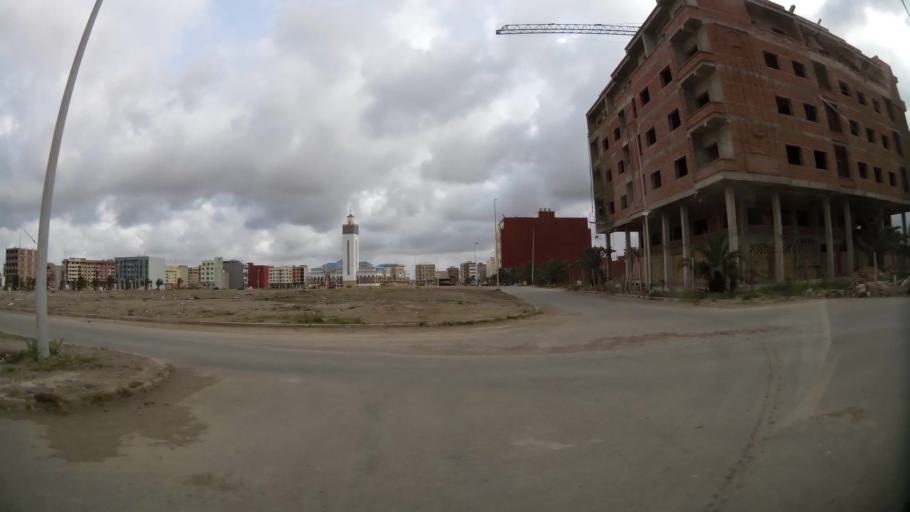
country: MA
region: Oriental
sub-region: Nador
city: Nador
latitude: 35.1549
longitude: -2.9192
